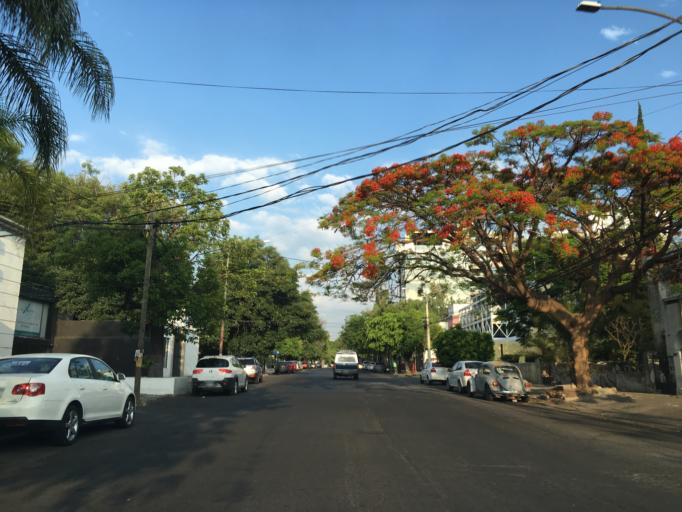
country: MX
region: Jalisco
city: Guadalajara
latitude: 20.6721
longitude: -103.3750
